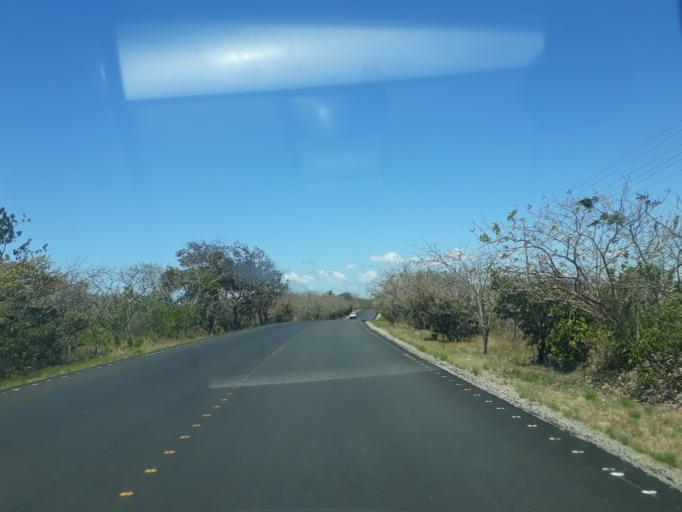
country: CR
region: Guanacaste
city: La Cruz
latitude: 10.9286
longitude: -85.6089
